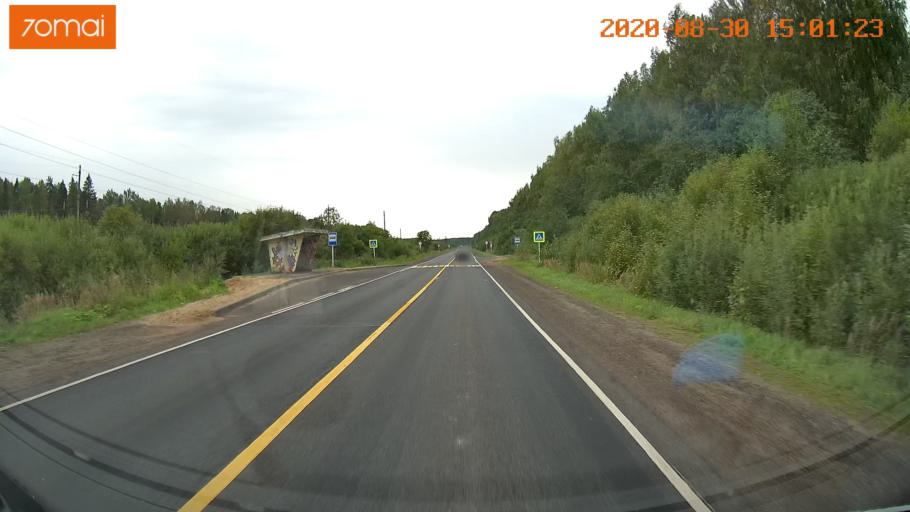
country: RU
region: Ivanovo
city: Staraya Vichuga
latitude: 57.3220
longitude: 41.9424
